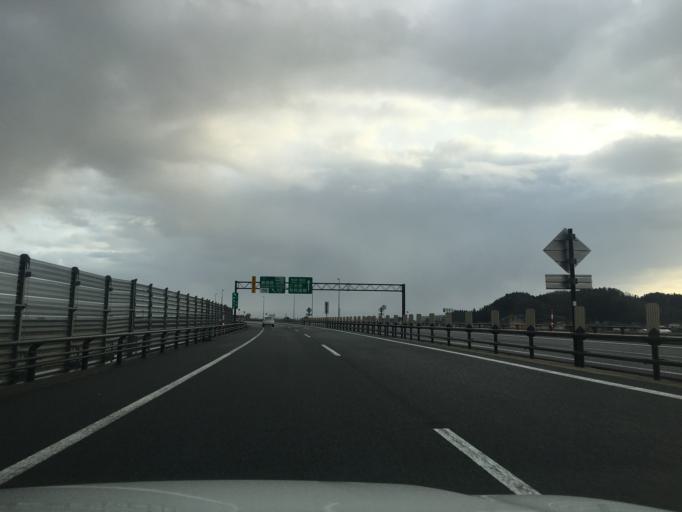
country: JP
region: Yamagata
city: Tsuruoka
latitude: 38.7132
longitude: 139.7538
